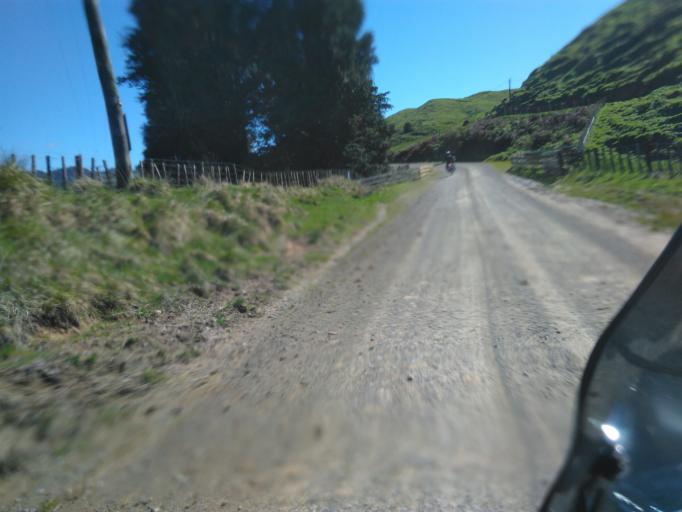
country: NZ
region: Bay of Plenty
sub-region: Opotiki District
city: Opotiki
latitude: -38.2855
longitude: 177.5432
